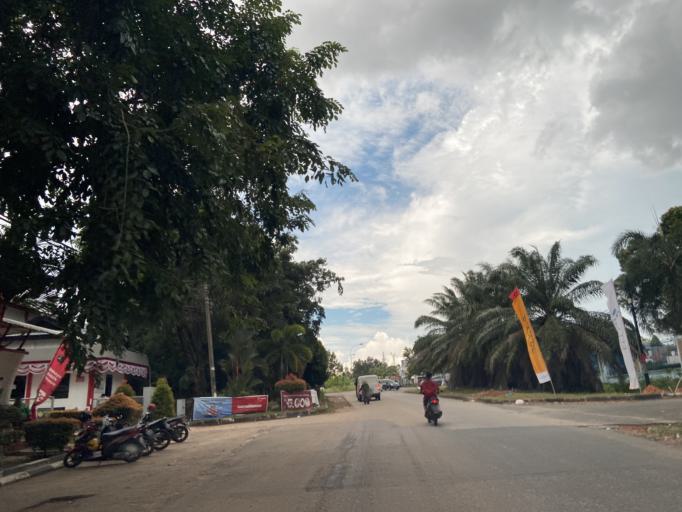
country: SG
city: Singapore
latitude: 1.1147
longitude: 104.0505
